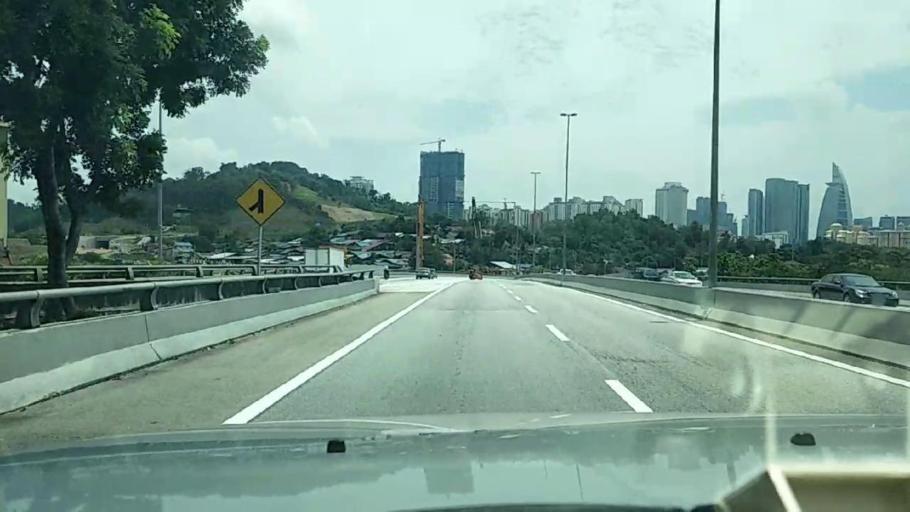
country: MY
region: Kuala Lumpur
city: Kuala Lumpur
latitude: 3.0938
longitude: 101.6704
